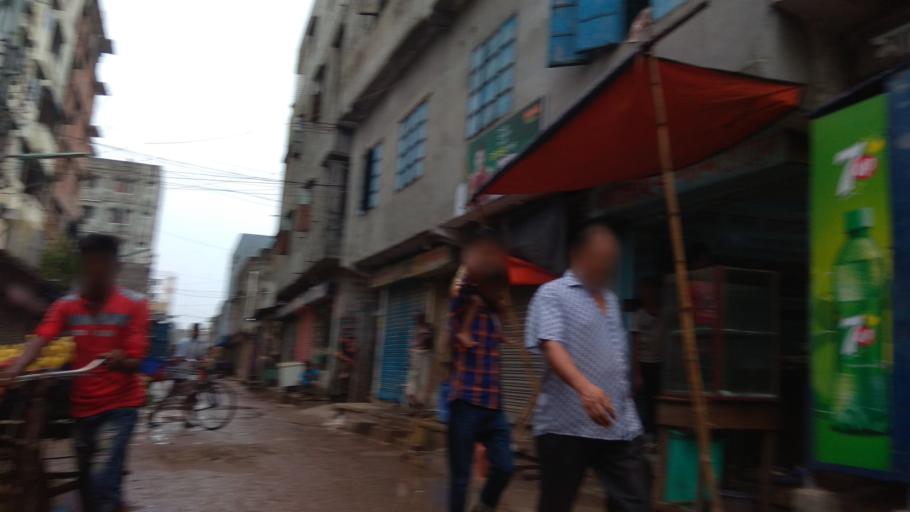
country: BD
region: Dhaka
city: Tungi
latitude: 23.8211
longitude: 90.3755
